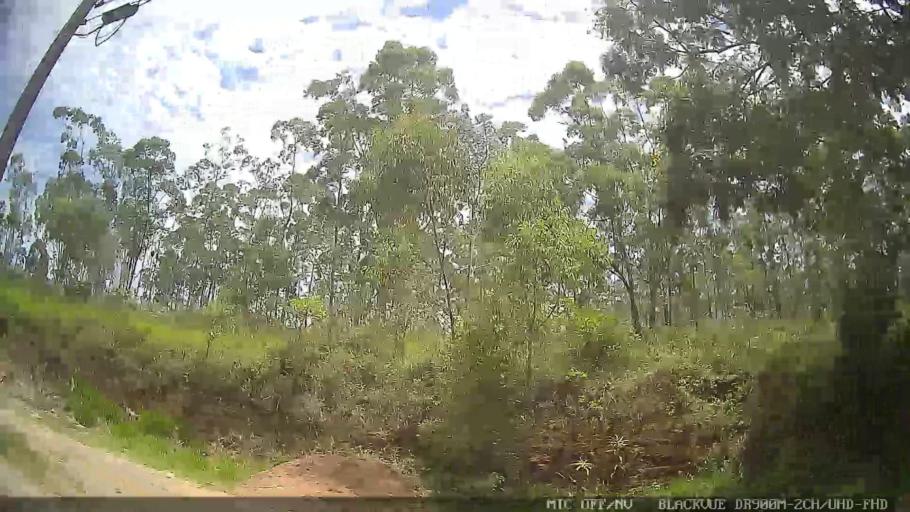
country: BR
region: Sao Paulo
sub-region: Biritiba-Mirim
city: Biritiba Mirim
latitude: -23.5488
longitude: -45.9658
